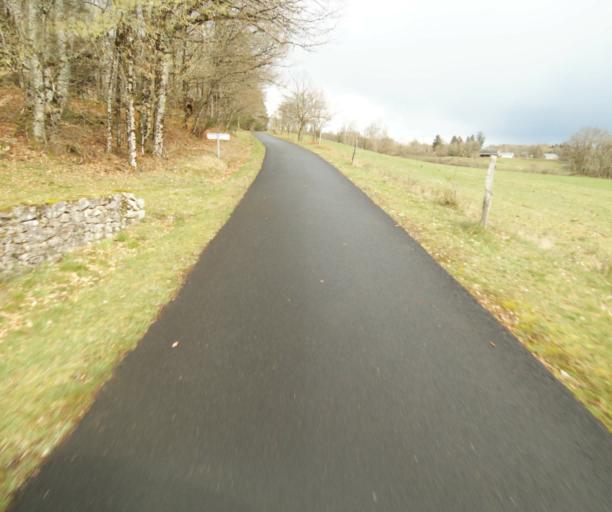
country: FR
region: Limousin
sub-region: Departement de la Correze
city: Saint-Privat
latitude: 45.2319
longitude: 1.9967
